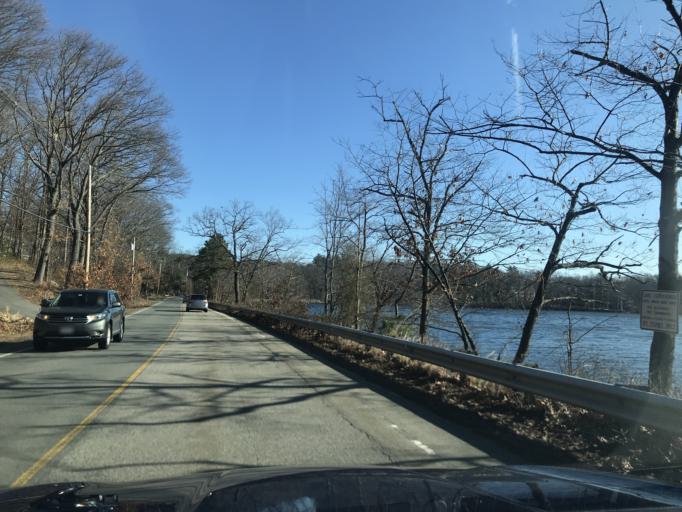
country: US
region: Massachusetts
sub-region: Essex County
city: North Andover
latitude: 42.7140
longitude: -71.1034
